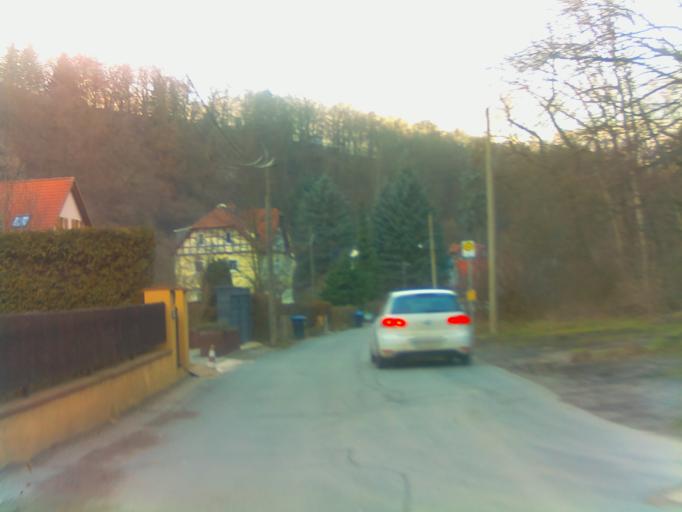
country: DE
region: Thuringia
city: Rudolstadt
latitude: 50.7029
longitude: 11.3438
